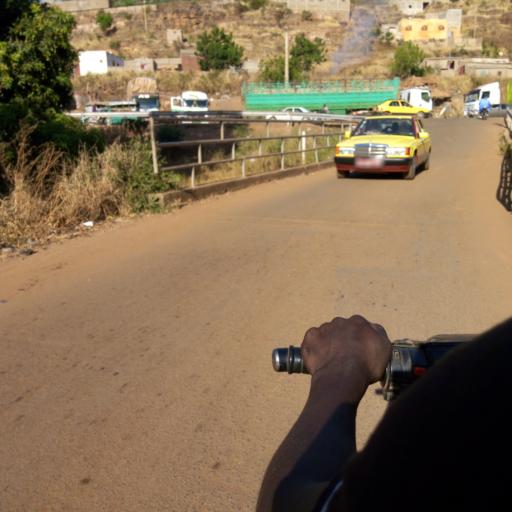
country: ML
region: Bamako
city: Bamako
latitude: 12.6605
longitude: -8.0352
